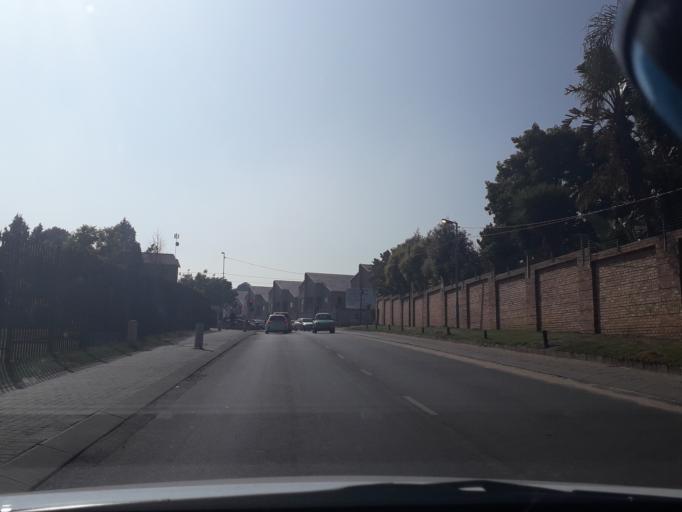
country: ZA
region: Gauteng
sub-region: City of Johannesburg Metropolitan Municipality
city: Diepsloot
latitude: -26.0458
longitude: 27.9688
